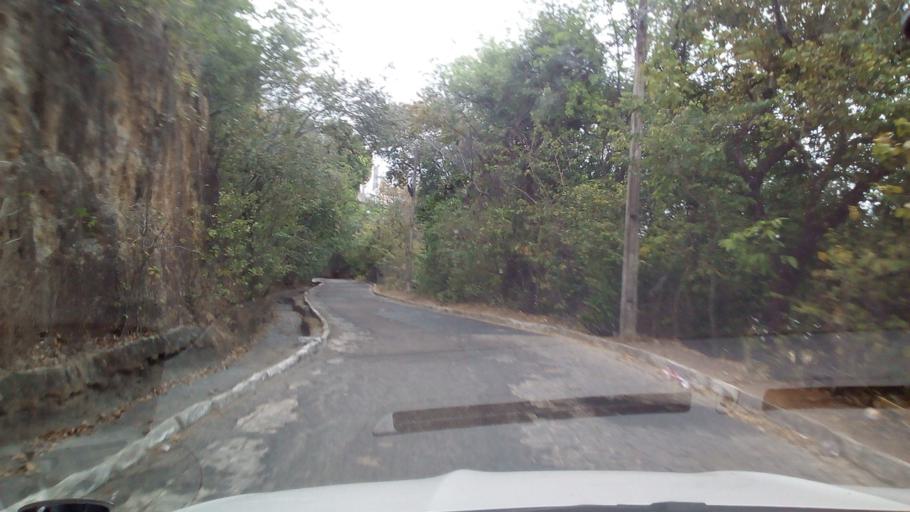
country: BR
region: Paraiba
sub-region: Joao Pessoa
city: Joao Pessoa
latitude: -7.1335
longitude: -34.8231
